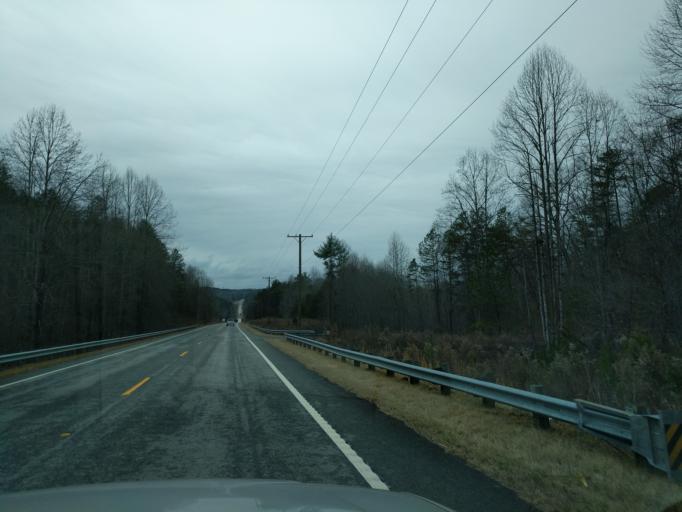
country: US
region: South Carolina
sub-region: Pickens County
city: Pickens
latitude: 34.9253
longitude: -82.8967
